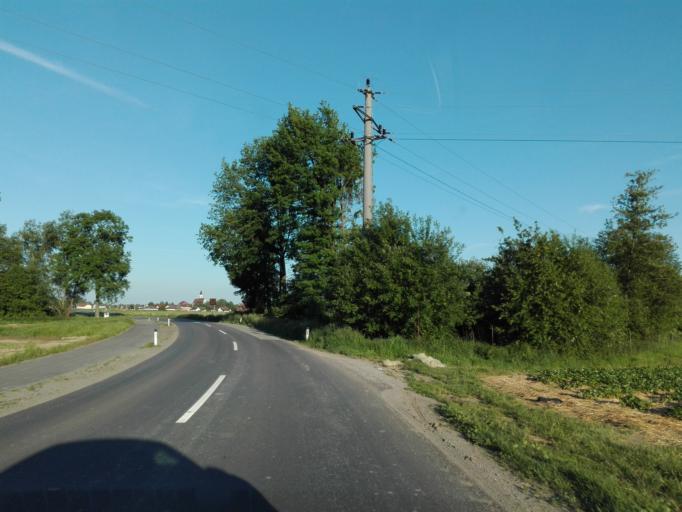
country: AT
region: Upper Austria
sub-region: Politischer Bezirk Urfahr-Umgebung
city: Feldkirchen an der Donau
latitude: 48.3183
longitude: 14.0007
